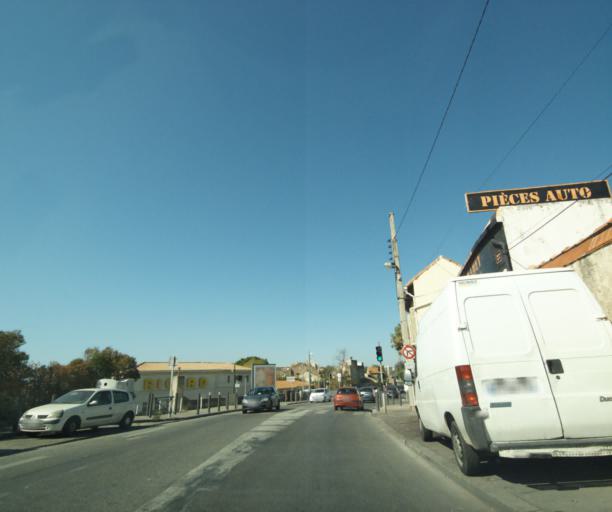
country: FR
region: Provence-Alpes-Cote d'Azur
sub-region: Departement des Bouches-du-Rhone
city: Marseille 14
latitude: 43.3378
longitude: 5.3942
